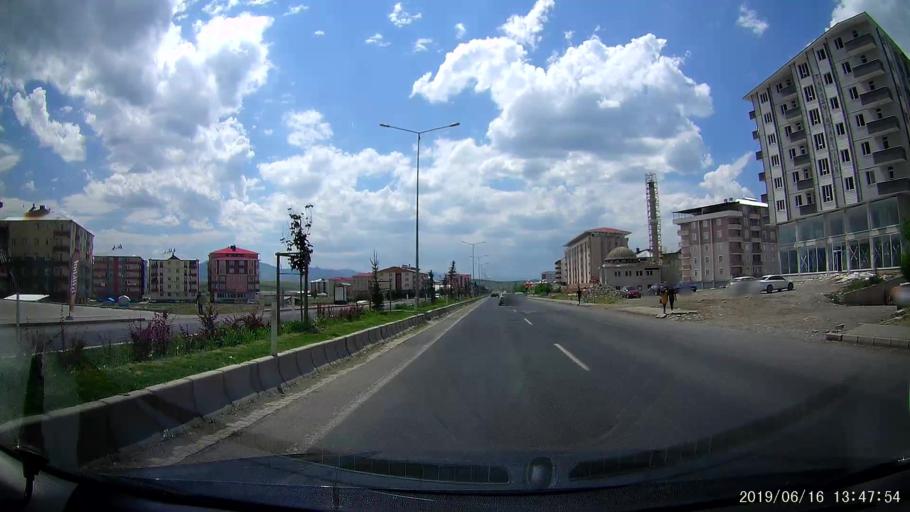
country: TR
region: Agri
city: Agri
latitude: 39.7143
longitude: 43.0169
